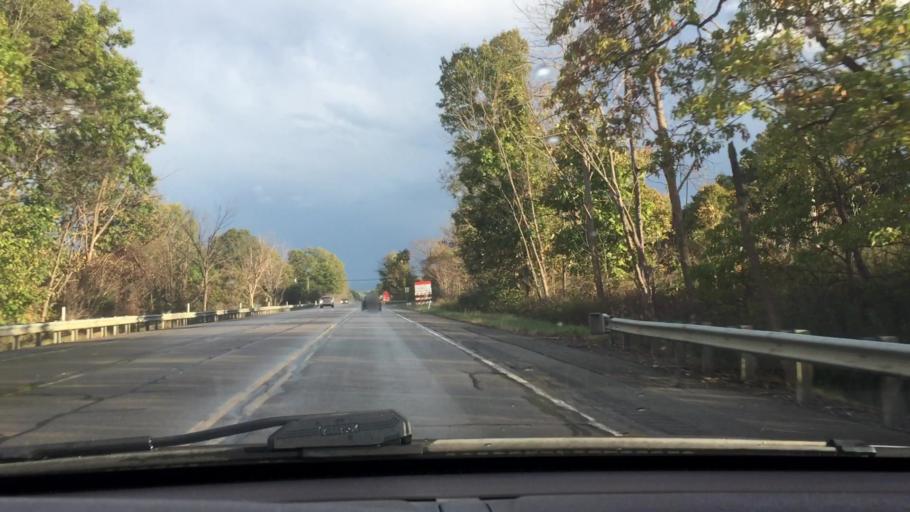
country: US
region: Pennsylvania
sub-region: Lawrence County
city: Oakwood
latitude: 41.0571
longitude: -80.4469
